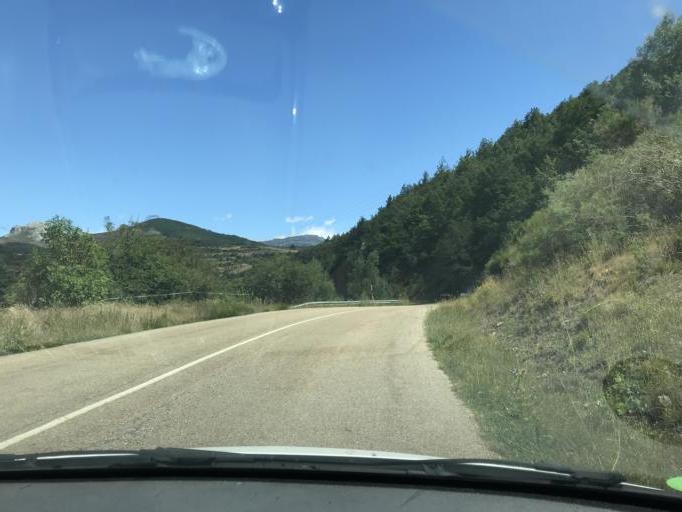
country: ES
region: Castille and Leon
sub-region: Provincia de Palencia
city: Polentinos
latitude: 42.9841
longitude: -4.4948
